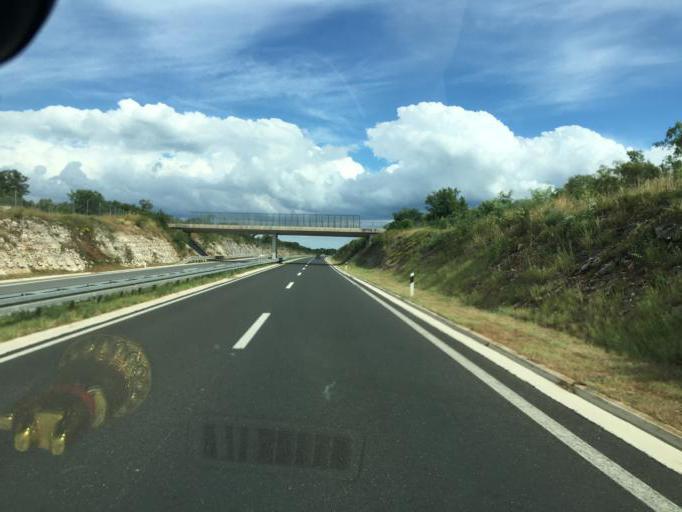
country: HR
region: Istarska
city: Vodnjan
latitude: 45.0915
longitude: 13.8283
